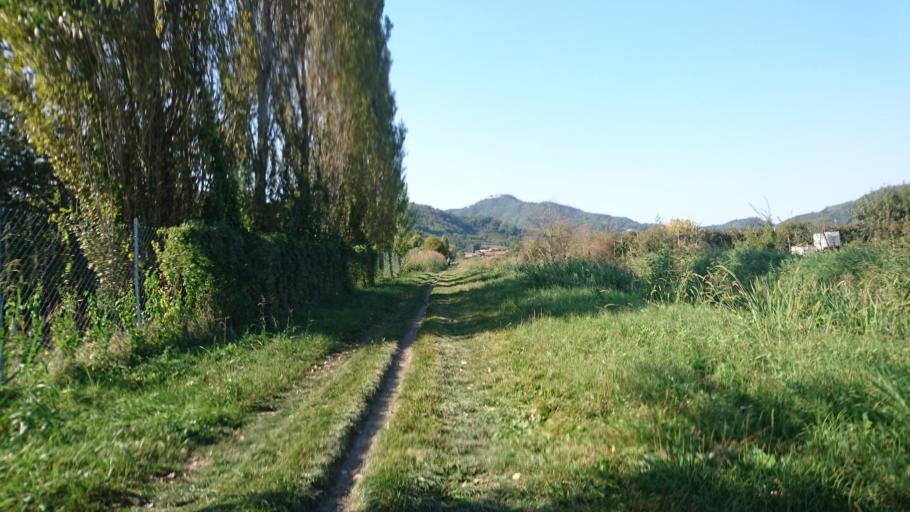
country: IT
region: Veneto
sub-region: Provincia di Padova
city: Galzignano
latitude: 45.2943
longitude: 11.7473
